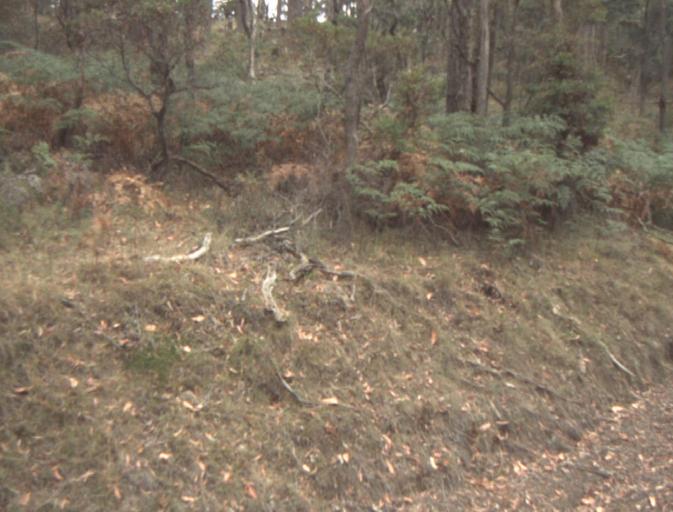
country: AU
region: Tasmania
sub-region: Northern Midlands
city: Evandale
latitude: -41.4927
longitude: 147.5477
